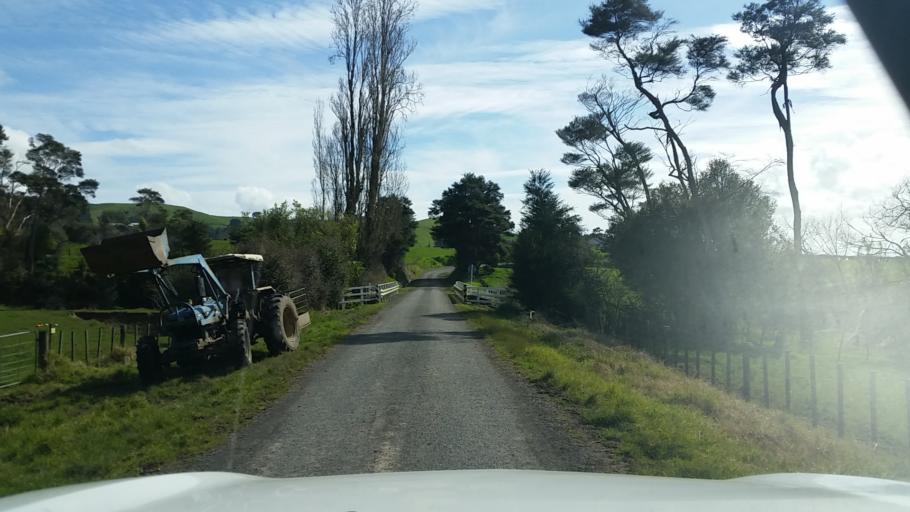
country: NZ
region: Waikato
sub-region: Hauraki District
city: Ngatea
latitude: -37.4389
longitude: 175.4797
